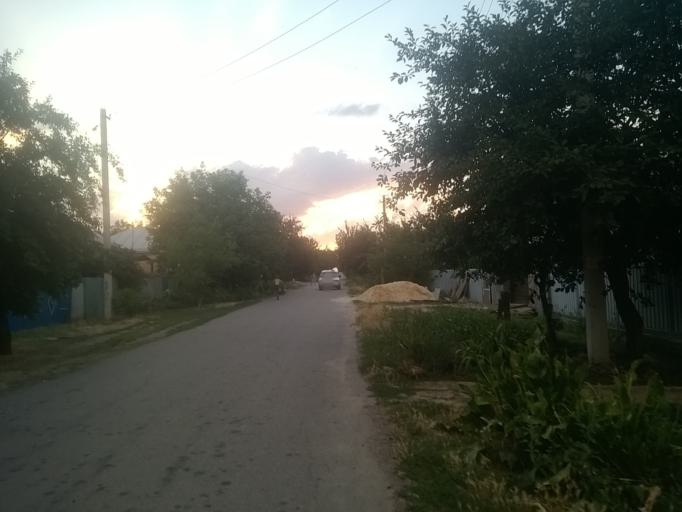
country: RU
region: Rostov
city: Donetsk
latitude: 48.3325
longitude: 39.9561
